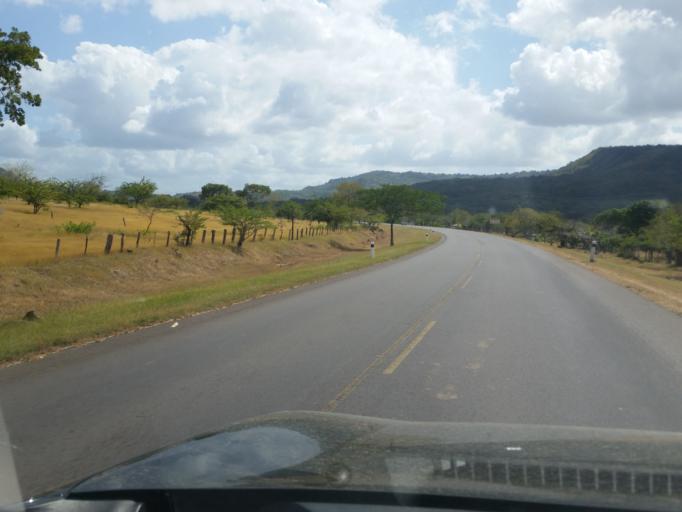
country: NI
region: Chontales
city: Comalapa
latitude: 12.1981
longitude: -85.6237
